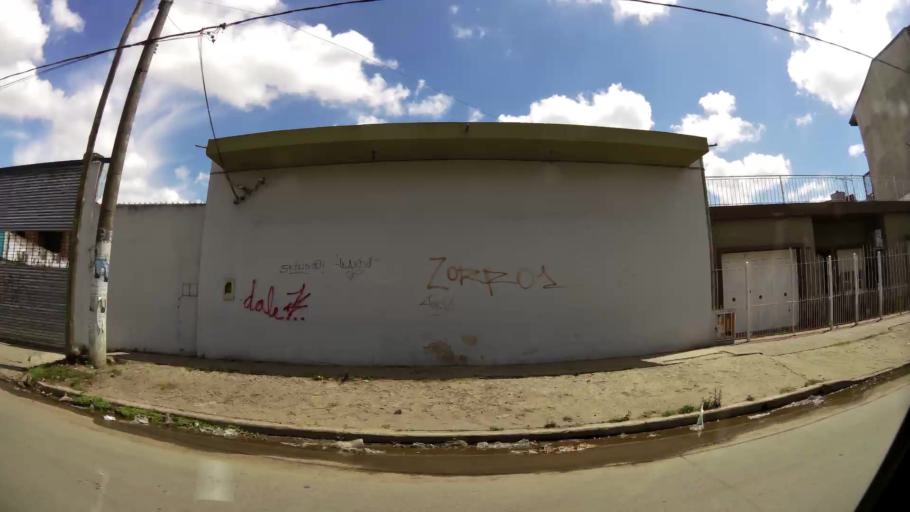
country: AR
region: Buenos Aires
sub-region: Partido de Quilmes
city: Quilmes
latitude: -34.8078
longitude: -58.2449
